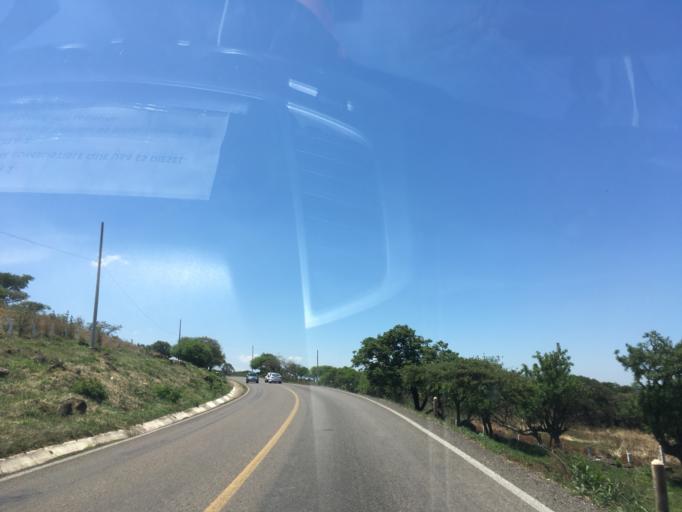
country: MX
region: Michoacan
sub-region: Tuxpan
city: La Soledad
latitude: 19.5072
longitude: -100.4685
